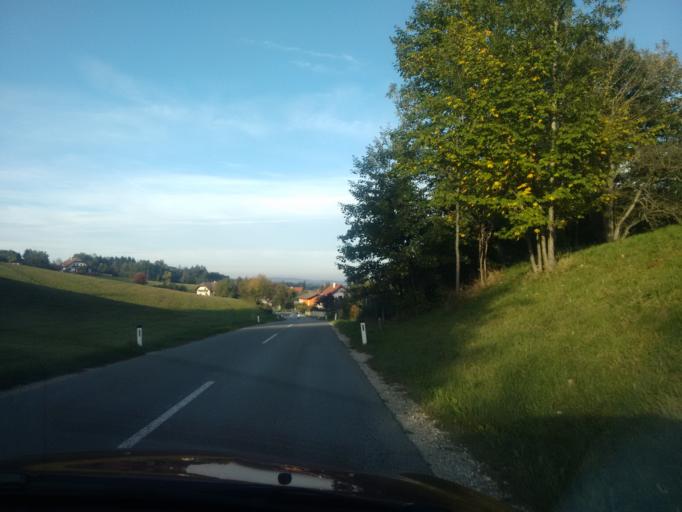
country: AT
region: Upper Austria
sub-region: Politischer Bezirk Vocklabruck
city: Wolfsegg am Hausruck
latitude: 48.1136
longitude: 13.6827
